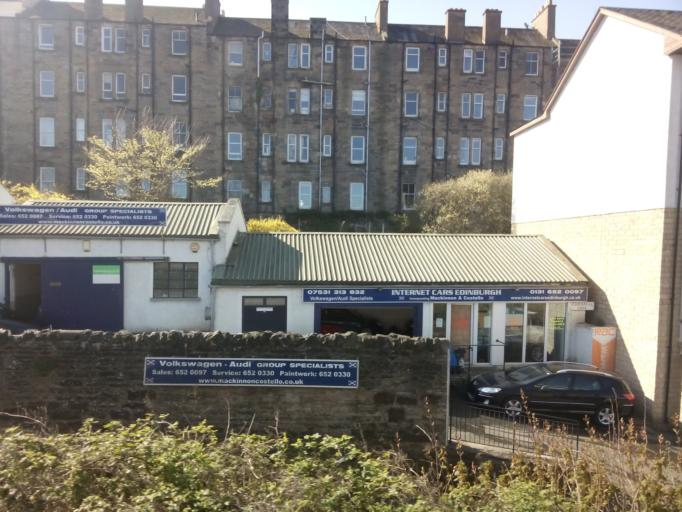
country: GB
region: Scotland
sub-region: West Lothian
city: Seafield
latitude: 55.9553
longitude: -3.1599
